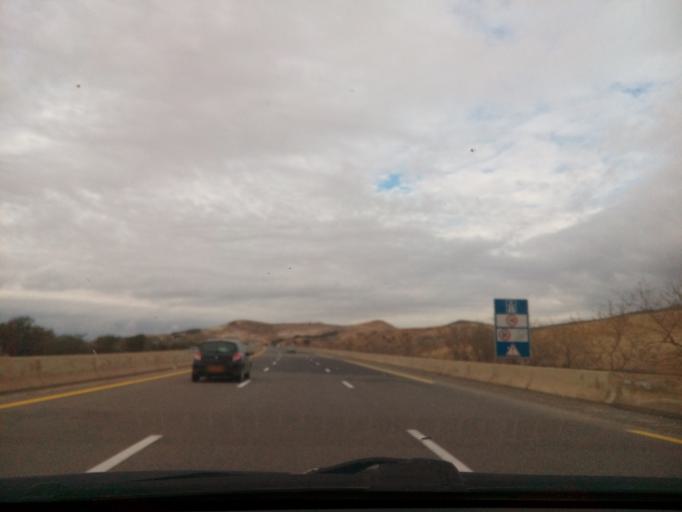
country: DZ
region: Sidi Bel Abbes
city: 'Ain el Berd
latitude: 35.4564
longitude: -0.3883
